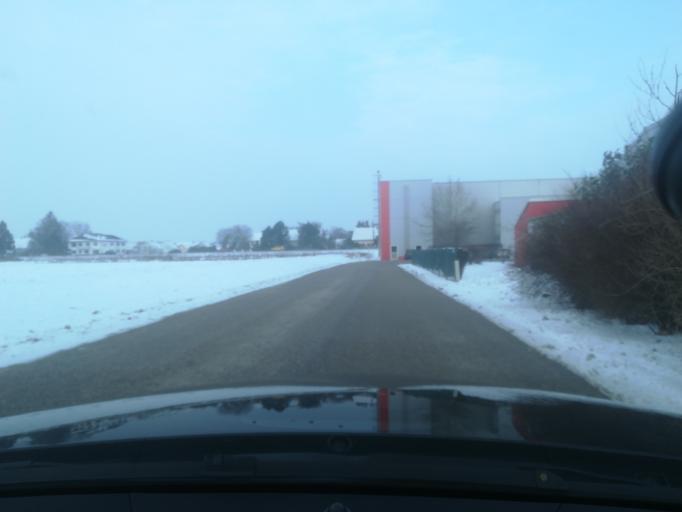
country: AT
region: Upper Austria
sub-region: Wels-Land
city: Marchtrenk
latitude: 48.1939
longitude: 14.1351
